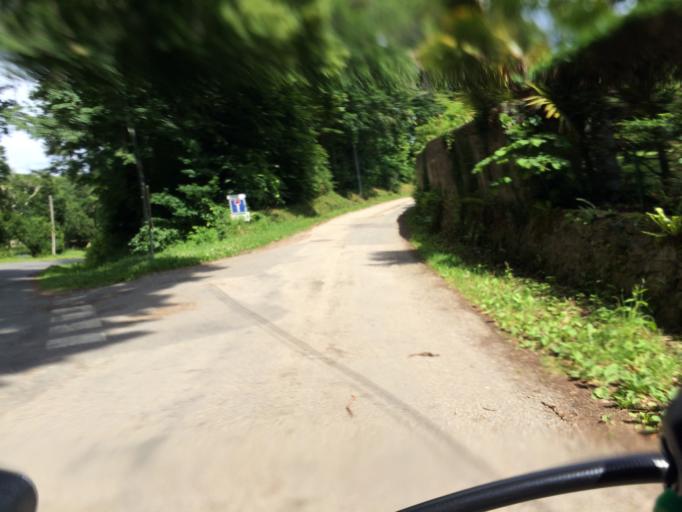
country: FR
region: Brittany
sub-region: Departement du Finistere
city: Logonna-Daoulas
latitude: 48.3160
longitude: -4.2910
